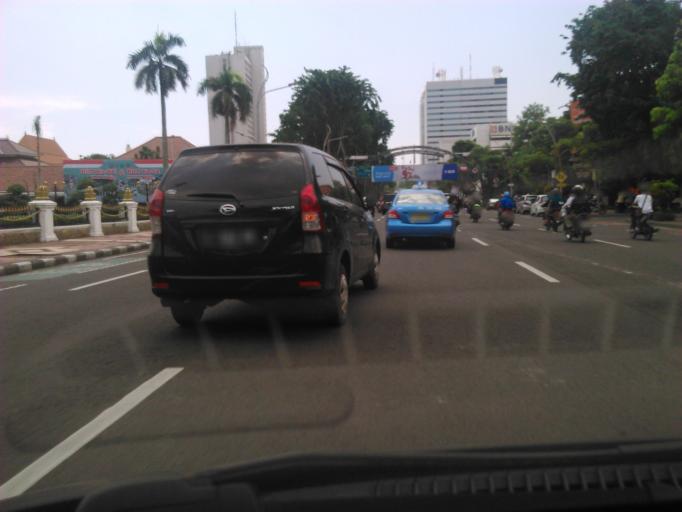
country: ID
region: East Java
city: Pacarkeling
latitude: -7.2635
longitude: 112.7429
